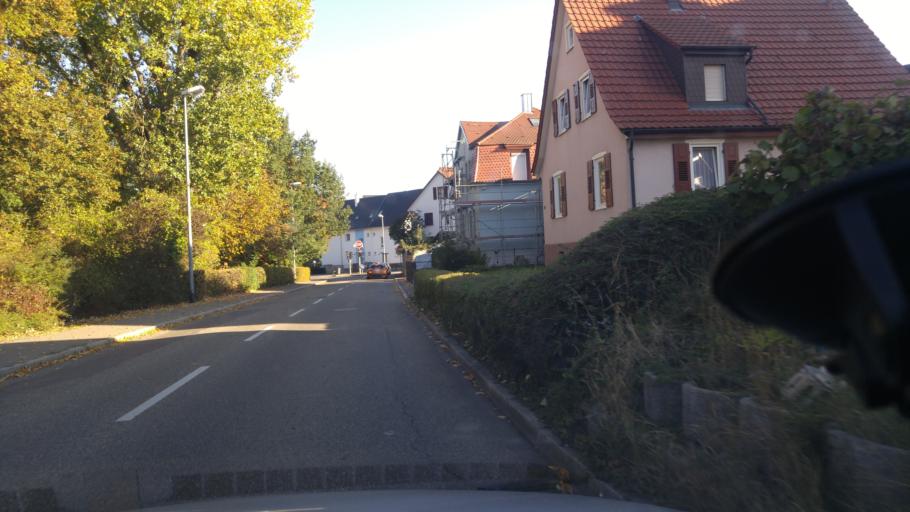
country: DE
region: Baden-Wuerttemberg
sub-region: Regierungsbezirk Stuttgart
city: Ditzingen
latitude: 48.8254
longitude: 9.0701
